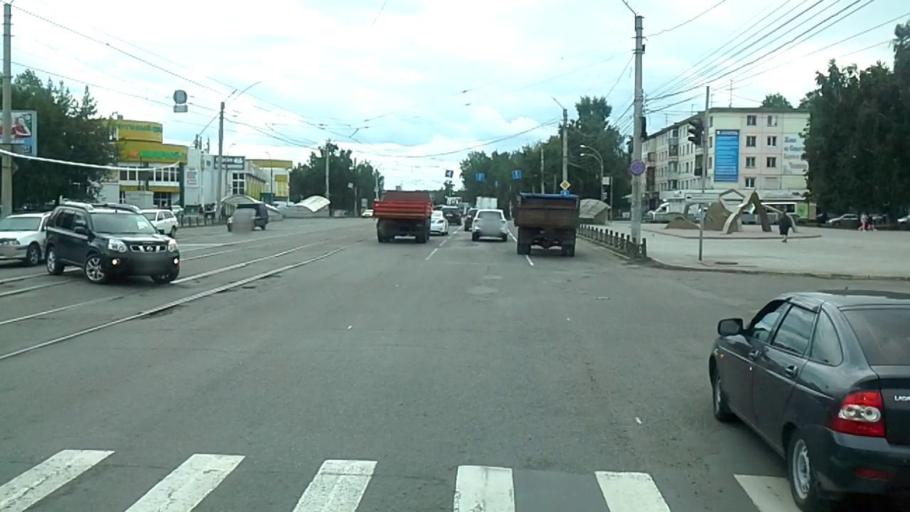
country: RU
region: Altai Krai
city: Biysk
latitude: 52.5418
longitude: 85.2192
